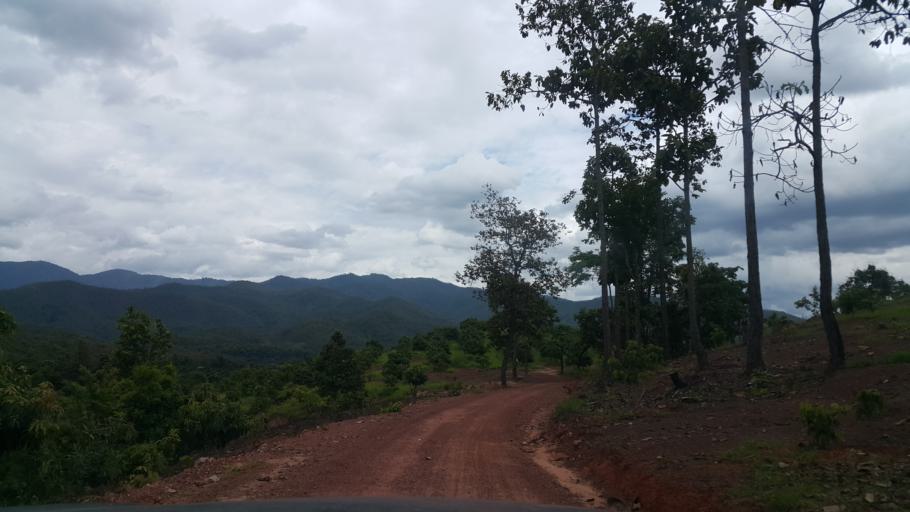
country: TH
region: Chiang Mai
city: Mae Taeng
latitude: 19.2204
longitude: 98.9966
